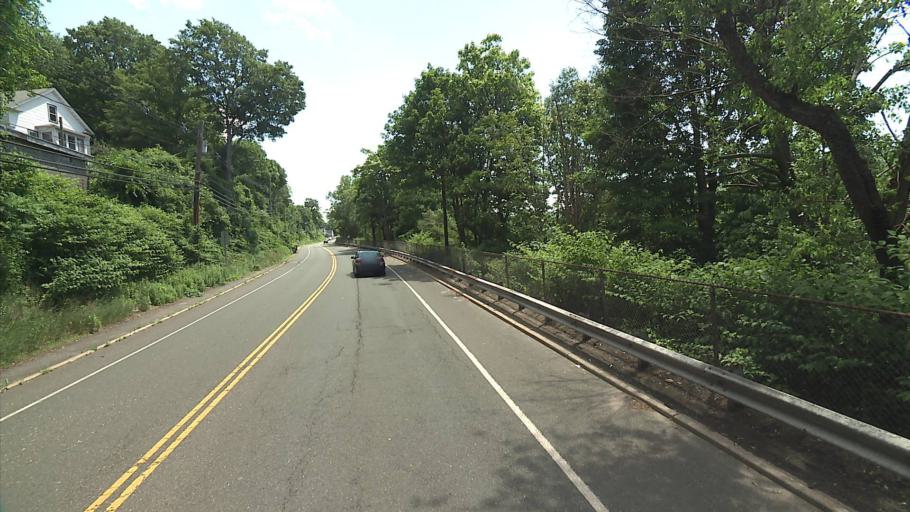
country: US
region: Connecticut
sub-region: New Haven County
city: Naugatuck
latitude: 41.4844
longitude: -73.0499
